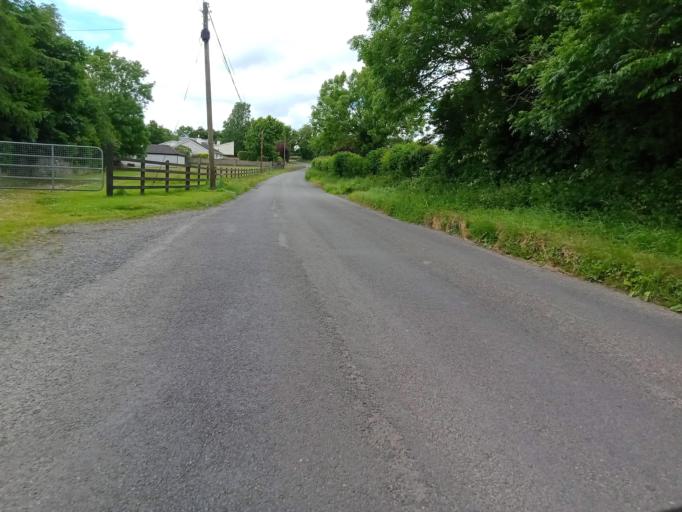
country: IE
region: Leinster
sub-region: Kilkenny
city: Kilkenny
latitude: 52.6912
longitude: -7.2497
